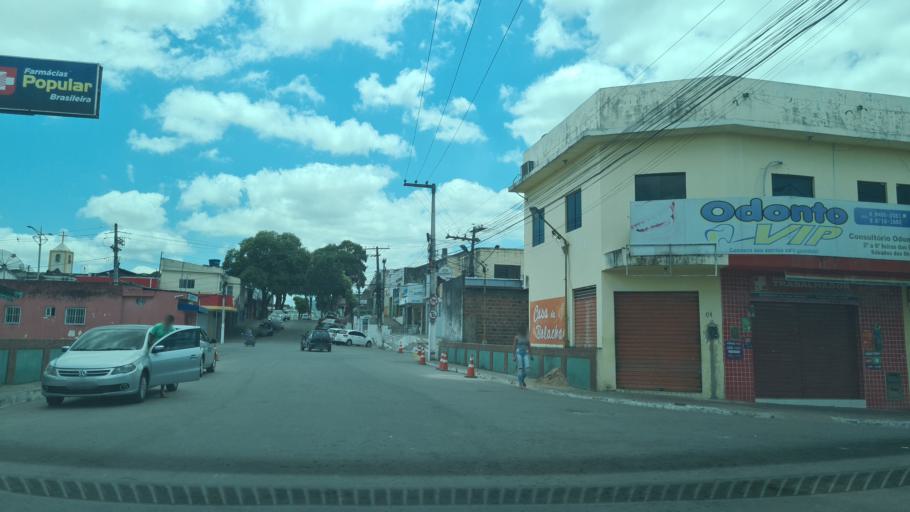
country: BR
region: Alagoas
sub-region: Uniao Dos Palmares
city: Uniao dos Palmares
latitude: -9.1574
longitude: -36.0325
